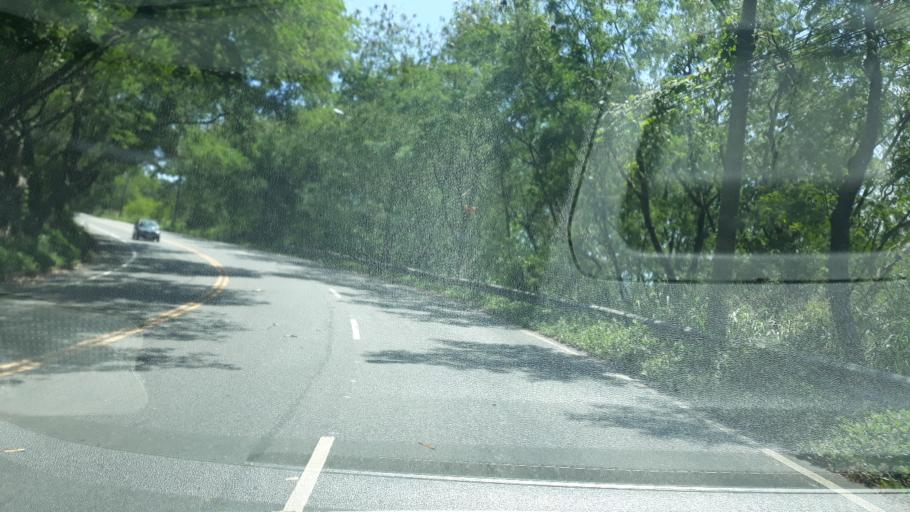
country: BR
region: Rio de Janeiro
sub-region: Nilopolis
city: Nilopolis
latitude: -23.0095
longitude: -43.5134
